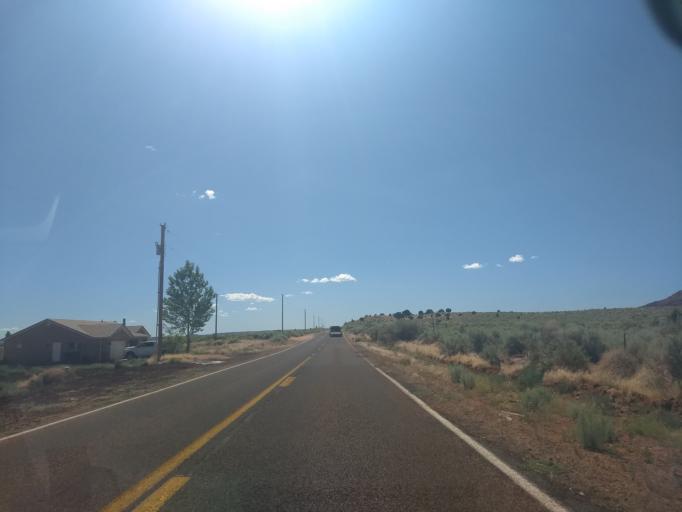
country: US
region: Arizona
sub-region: Mohave County
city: Colorado City
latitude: 36.9469
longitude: -112.9162
